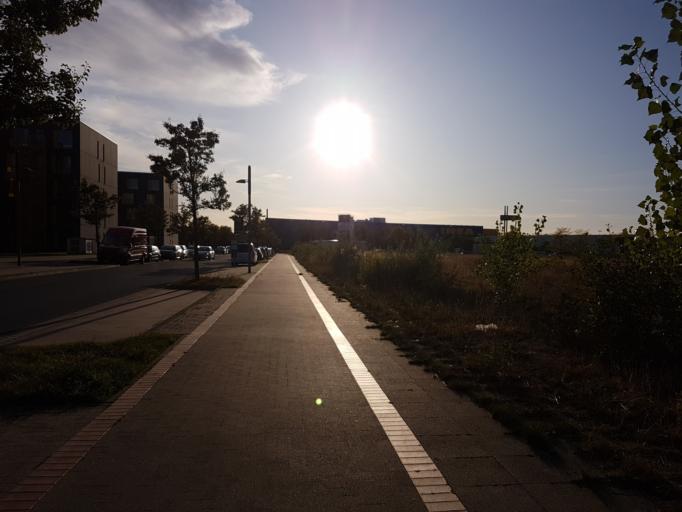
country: DE
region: Lower Saxony
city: Laatzen
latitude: 52.3140
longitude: 9.8220
